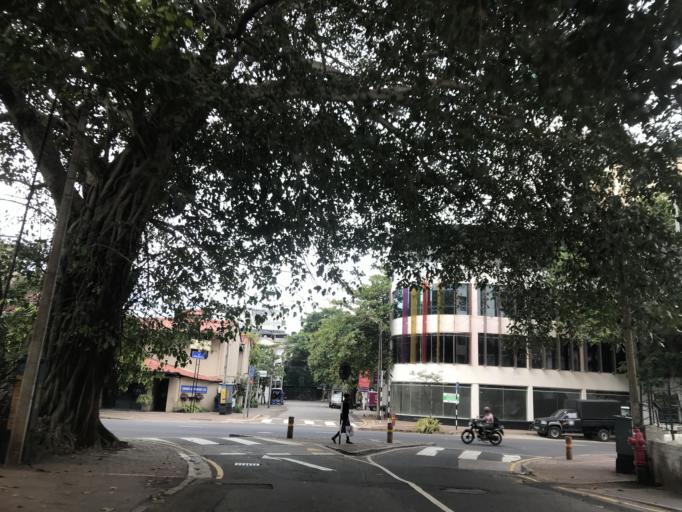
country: LK
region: Western
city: Colombo
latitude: 6.8988
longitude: 79.8561
